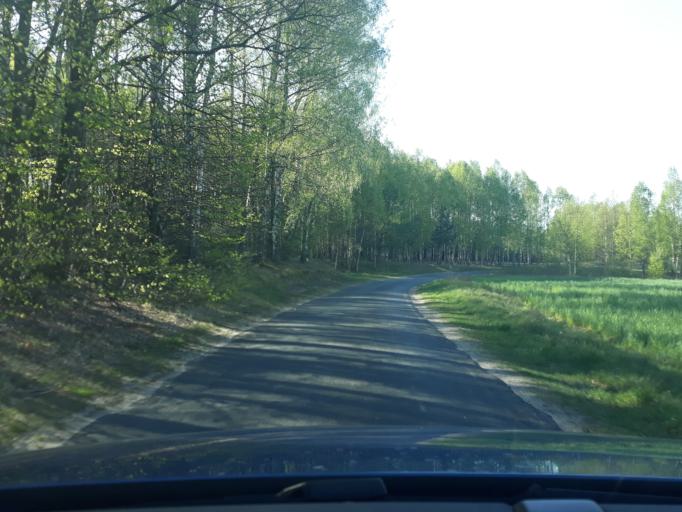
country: PL
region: Pomeranian Voivodeship
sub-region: Powiat czluchowski
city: Przechlewo
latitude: 53.8662
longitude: 17.3351
